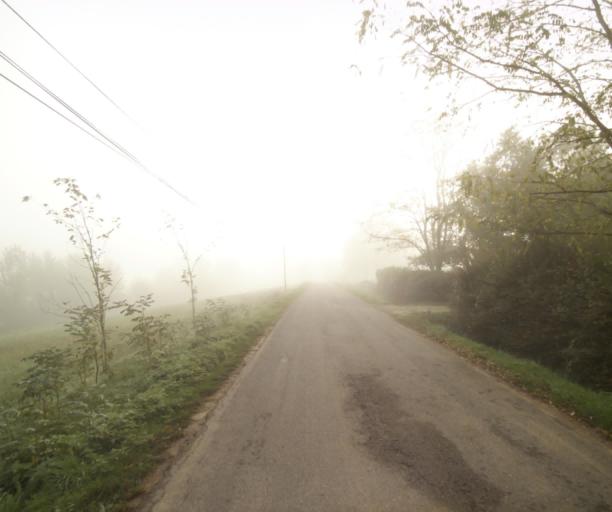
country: FR
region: Midi-Pyrenees
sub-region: Departement du Tarn-et-Garonne
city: Nohic
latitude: 43.9053
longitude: 1.4460
